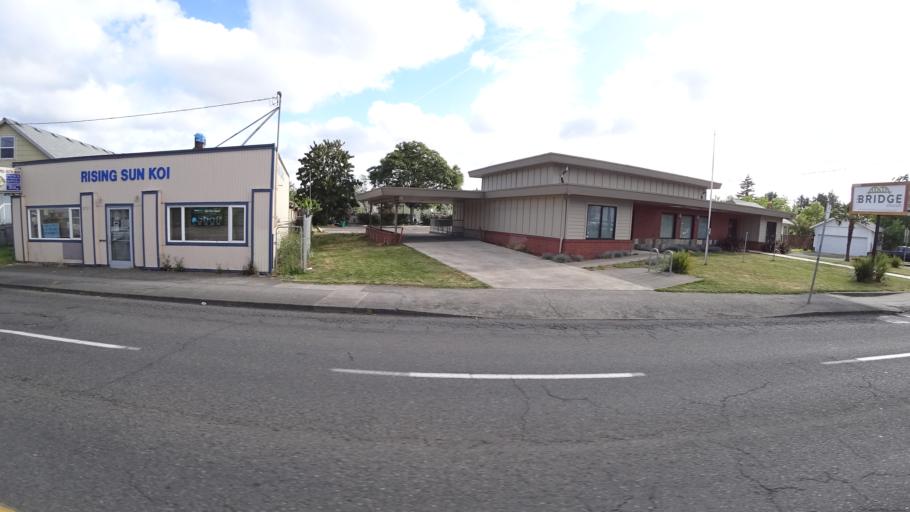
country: US
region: Oregon
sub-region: Multnomah County
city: Lents
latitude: 45.4810
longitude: -122.5726
